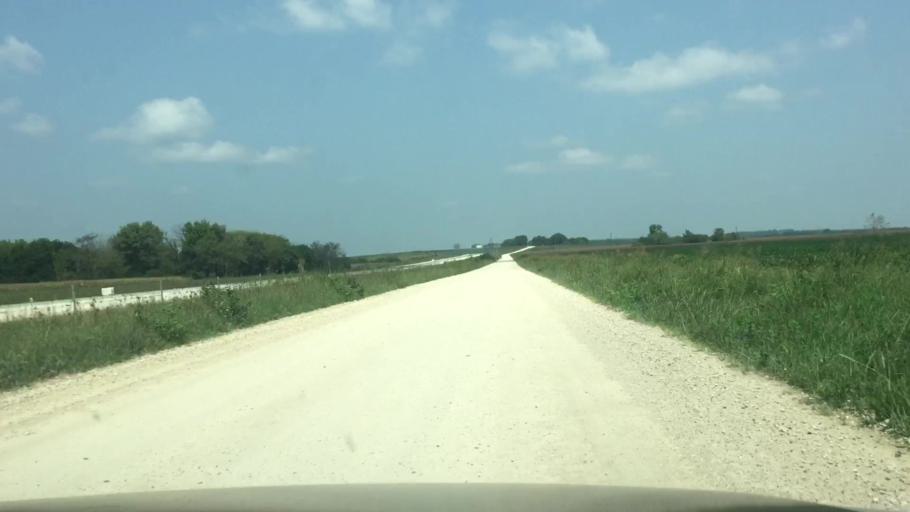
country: US
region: Kansas
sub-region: Allen County
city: Humboldt
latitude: 37.8402
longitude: -95.4093
